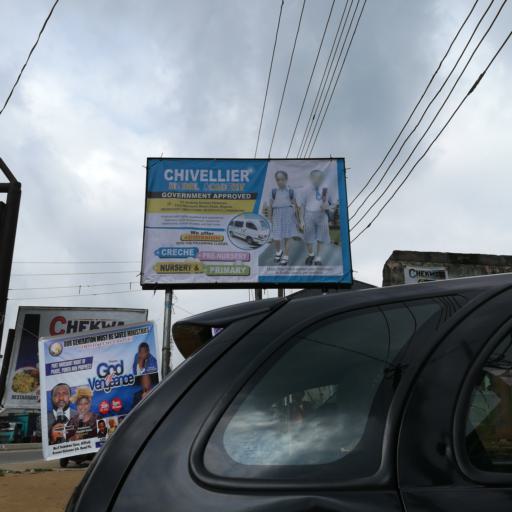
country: NG
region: Rivers
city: Port Harcourt
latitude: 4.8307
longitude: 7.0707
